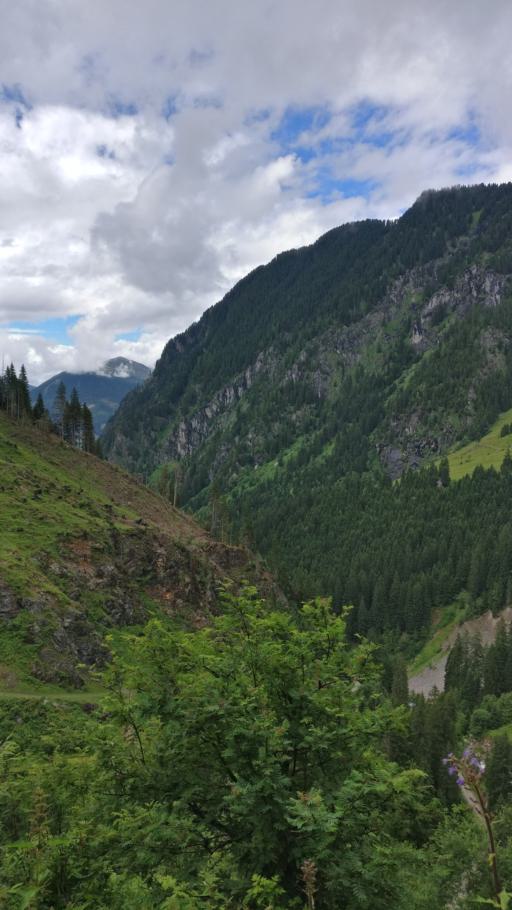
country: AT
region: Salzburg
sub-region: Politischer Bezirk Zell am See
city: Neukirchen am Grossvenediger
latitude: 47.1892
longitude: 12.2616
